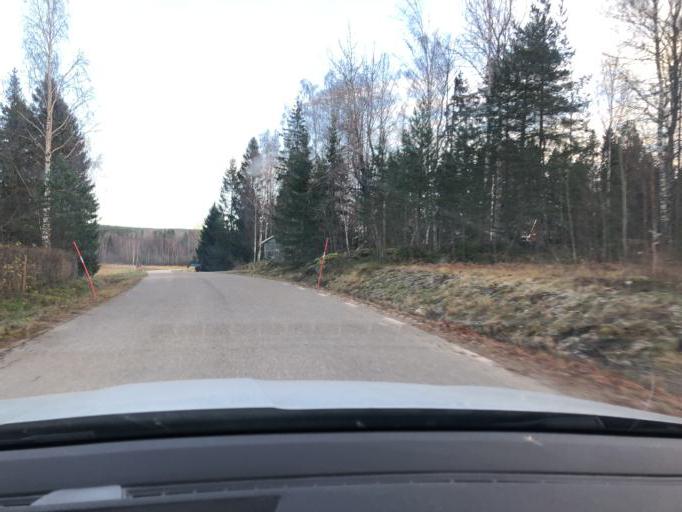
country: SE
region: Gaevleborg
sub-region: Hudiksvalls Kommun
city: Sorforsa
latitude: 61.7126
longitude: 16.9394
